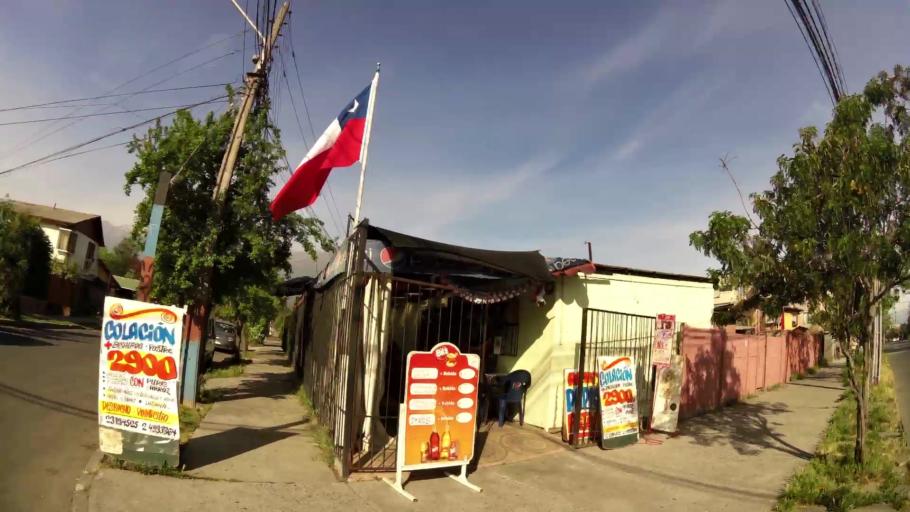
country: CL
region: Santiago Metropolitan
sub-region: Provincia de Santiago
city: Villa Presidente Frei, Nunoa, Santiago, Chile
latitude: -33.5343
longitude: -70.5777
